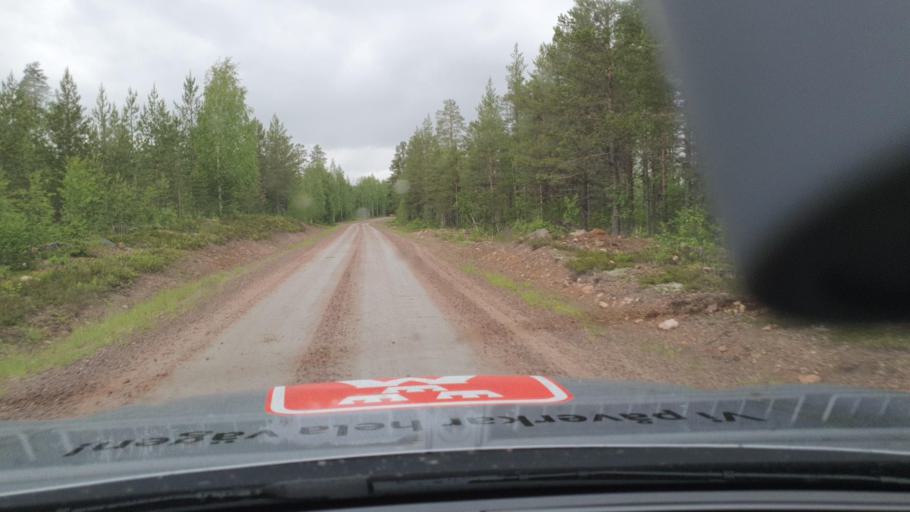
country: SE
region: Norrbotten
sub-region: Overkalix Kommun
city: OEverkalix
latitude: 66.6383
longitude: 22.7072
